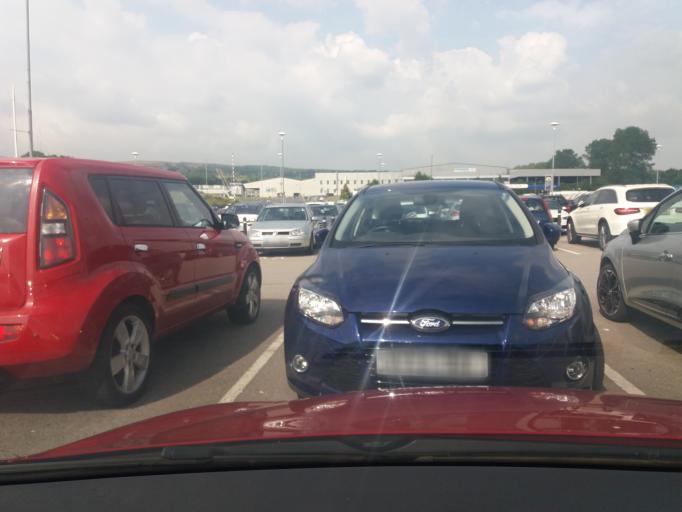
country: GB
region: England
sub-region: Borough of Bolton
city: Horwich
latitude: 53.5809
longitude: -2.5309
